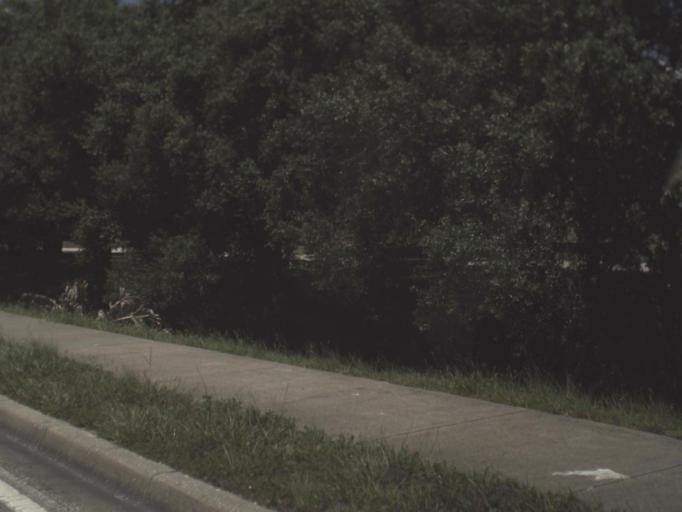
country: US
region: Florida
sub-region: Pinellas County
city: Pinellas Park
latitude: 27.8793
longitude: -82.7089
